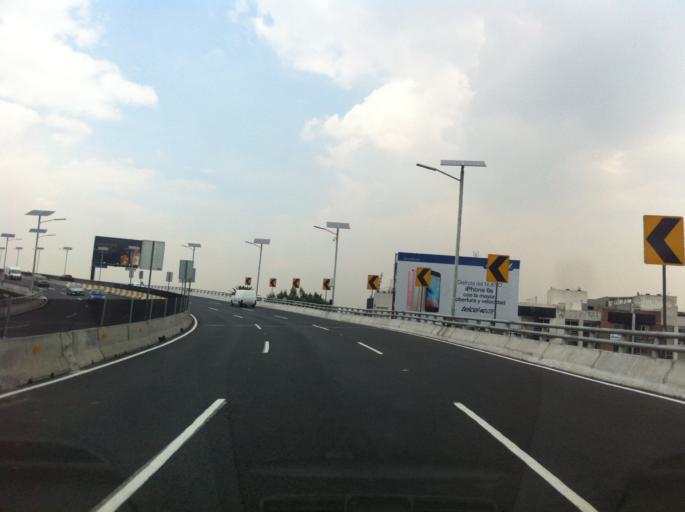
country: MX
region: Mexico City
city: Polanco
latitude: 19.3931
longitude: -99.1883
